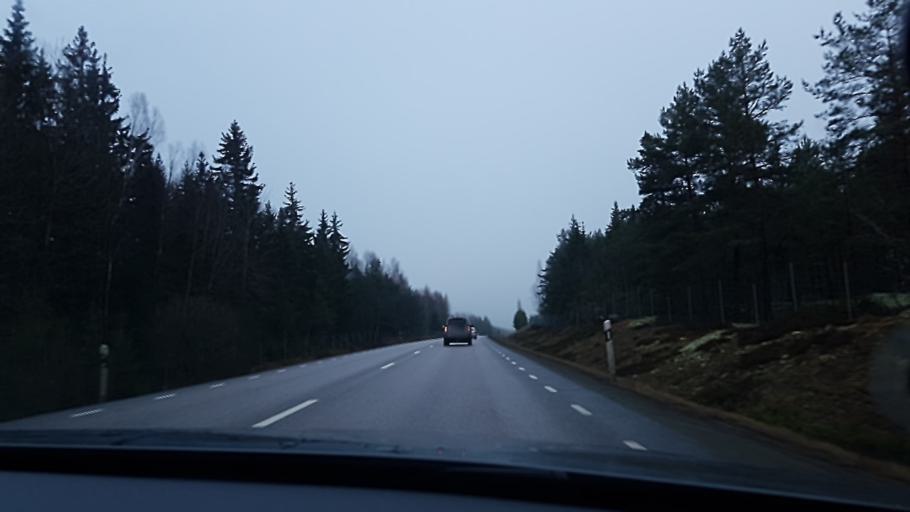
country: SE
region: Vaestra Goetaland
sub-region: Toreboda Kommun
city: Toereboda
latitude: 58.8248
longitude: 13.9878
